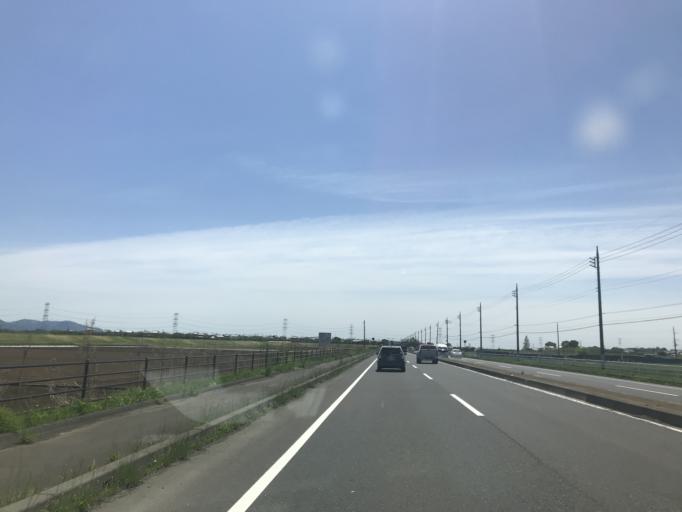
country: JP
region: Ibaraki
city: Shimodate
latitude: 36.2710
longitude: 139.9807
